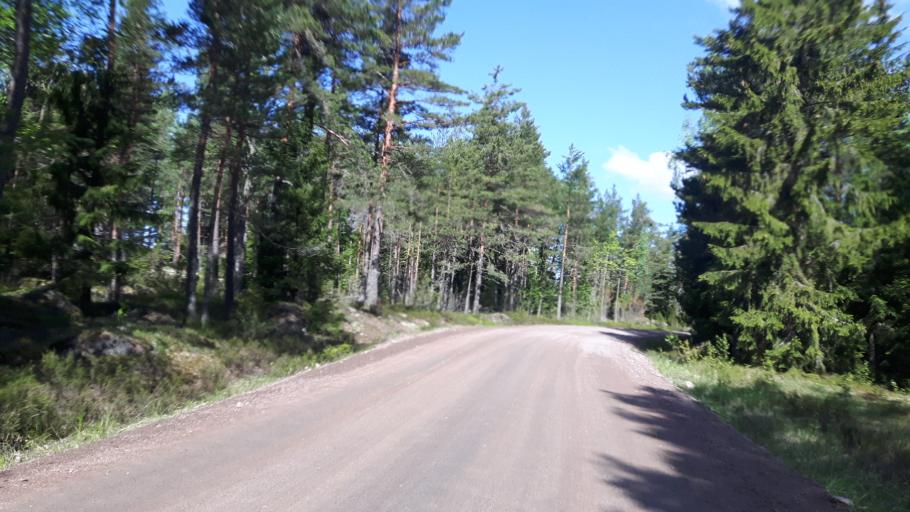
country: FI
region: Kymenlaakso
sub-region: Kotka-Hamina
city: Hamina
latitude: 60.5293
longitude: 27.2858
